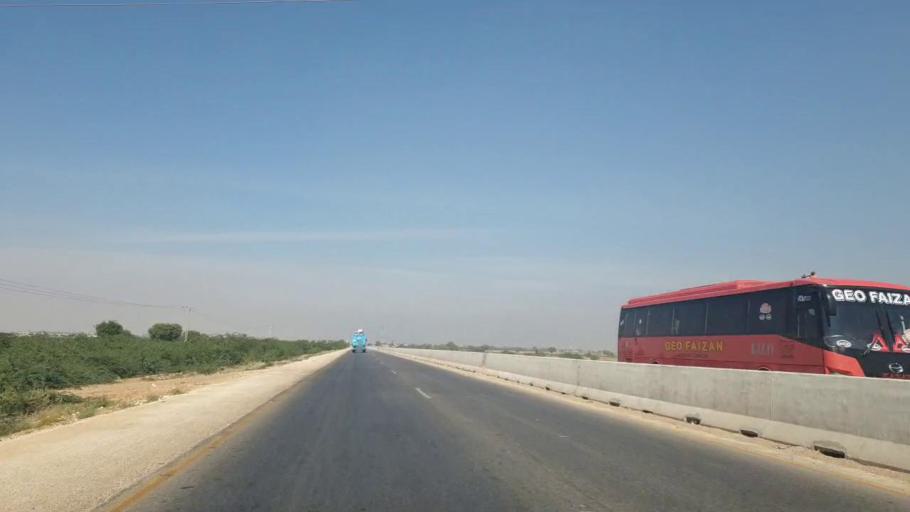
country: PK
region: Sindh
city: Matiari
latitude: 25.6349
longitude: 68.3016
